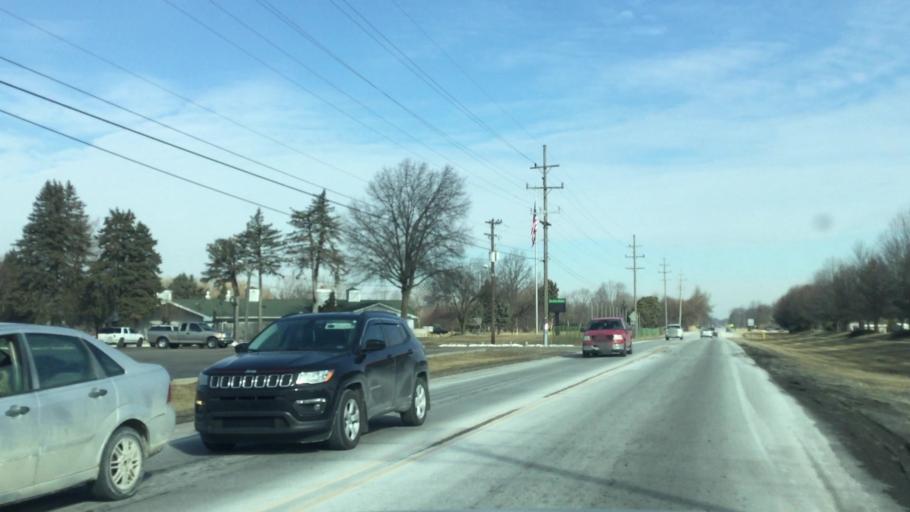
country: US
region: Michigan
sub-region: Wayne County
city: Flat Rock
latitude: 42.1523
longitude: -83.3055
